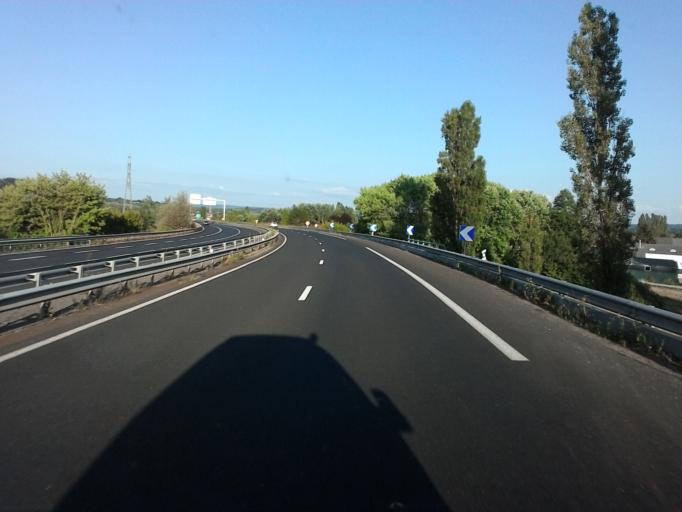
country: FR
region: Lorraine
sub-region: Departement des Vosges
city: Chavelot
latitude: 48.2260
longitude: 6.4313
